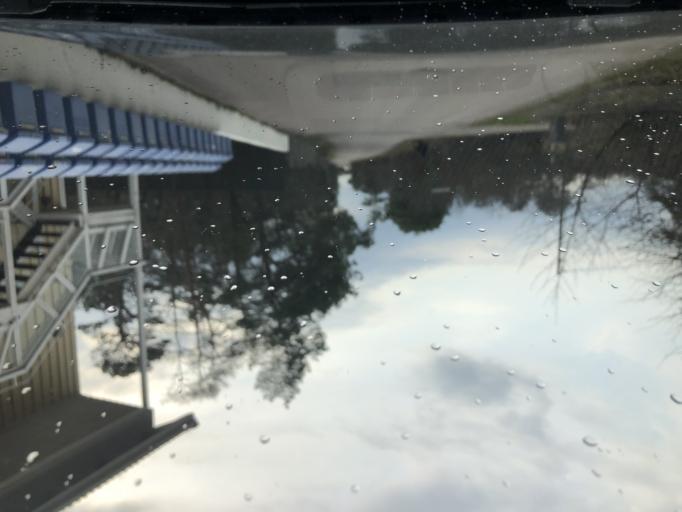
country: SE
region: Kalmar
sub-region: Borgholms Kommun
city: Borgholm
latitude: 57.2258
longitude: 16.9574
